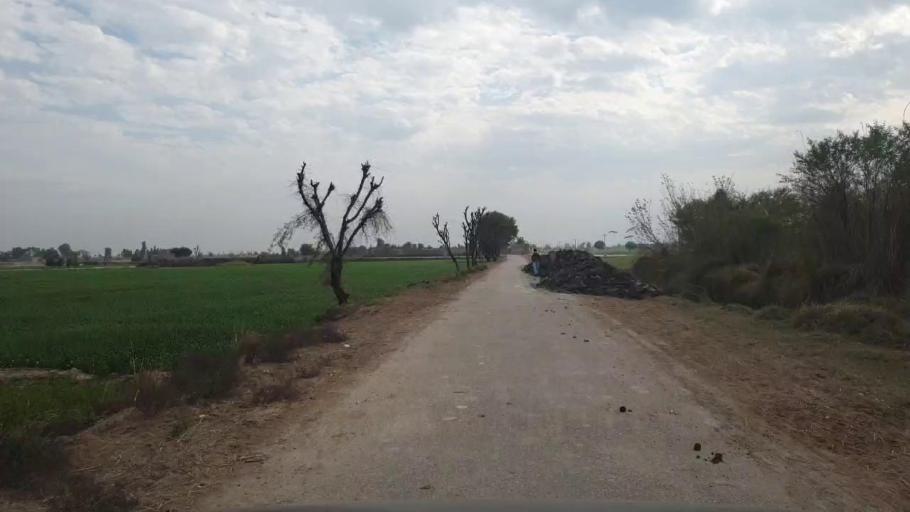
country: PK
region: Sindh
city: Hala
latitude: 26.0108
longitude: 68.4327
